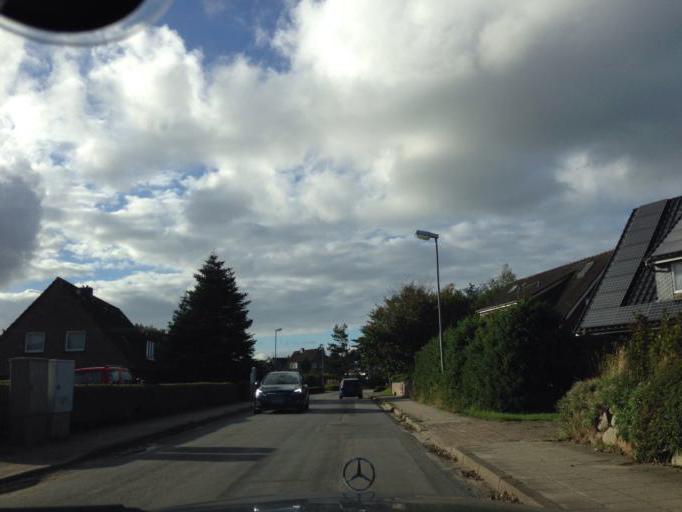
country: DE
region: Schleswig-Holstein
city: Wyk auf Fohr
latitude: 54.6939
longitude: 8.5574
